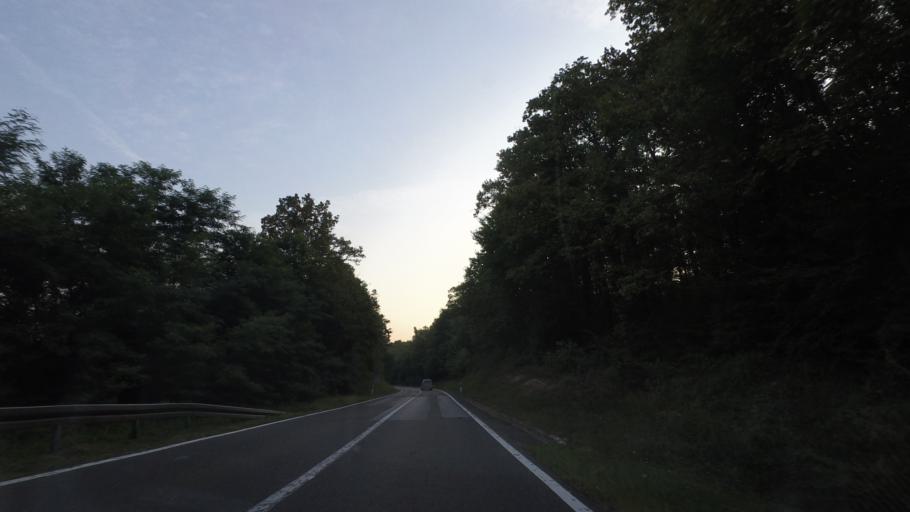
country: HR
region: Brodsko-Posavska
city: Cernik
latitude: 45.2792
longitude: 17.4034
